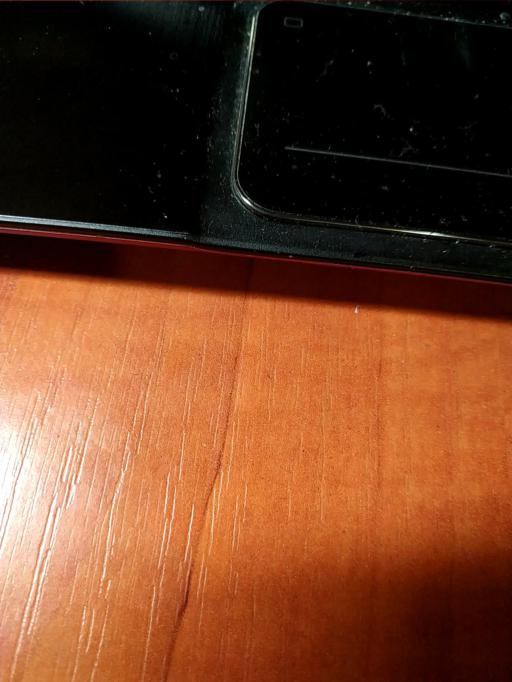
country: RU
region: Smolensk
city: Yartsevo
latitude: 55.4350
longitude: 32.7746
